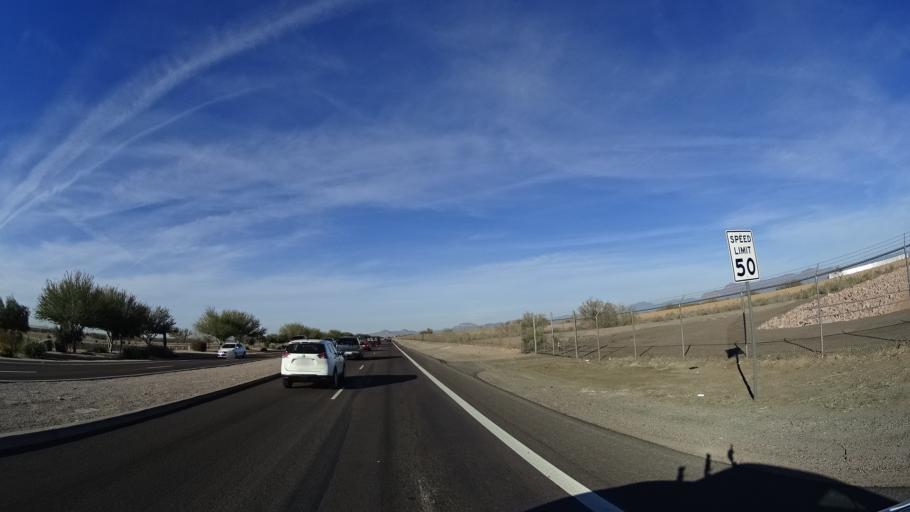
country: US
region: Arizona
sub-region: Maricopa County
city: Queen Creek
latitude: 33.2930
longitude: -111.6349
